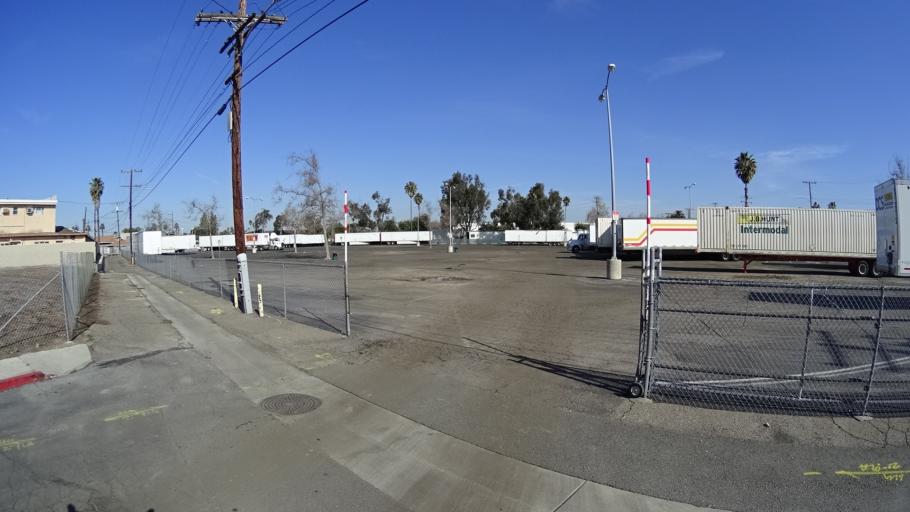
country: US
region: California
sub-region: Orange County
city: Anaheim
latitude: 33.8490
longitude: -117.9209
